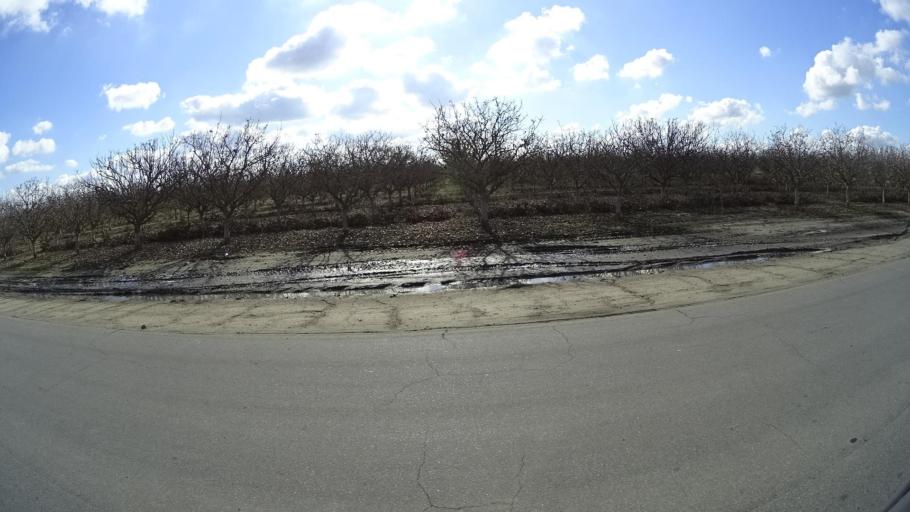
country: US
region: California
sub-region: Kern County
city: Wasco
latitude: 35.6742
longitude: -119.3244
